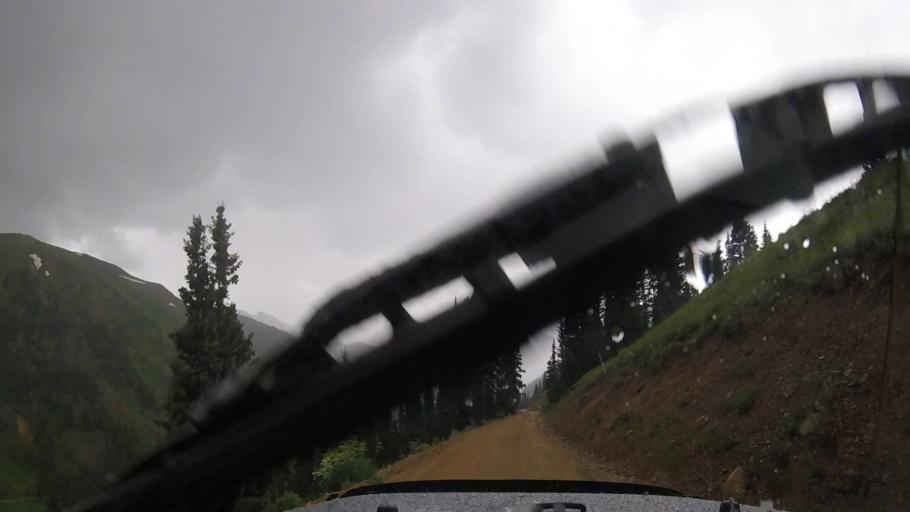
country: US
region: Colorado
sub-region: San Juan County
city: Silverton
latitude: 37.9094
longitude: -107.6450
